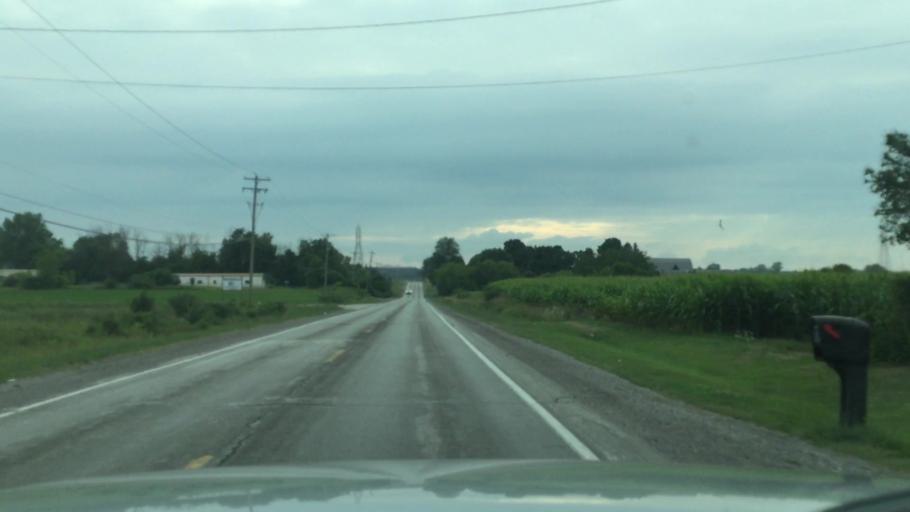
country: US
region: Michigan
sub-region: Saginaw County
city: Bridgeport
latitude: 43.3358
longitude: -83.8260
